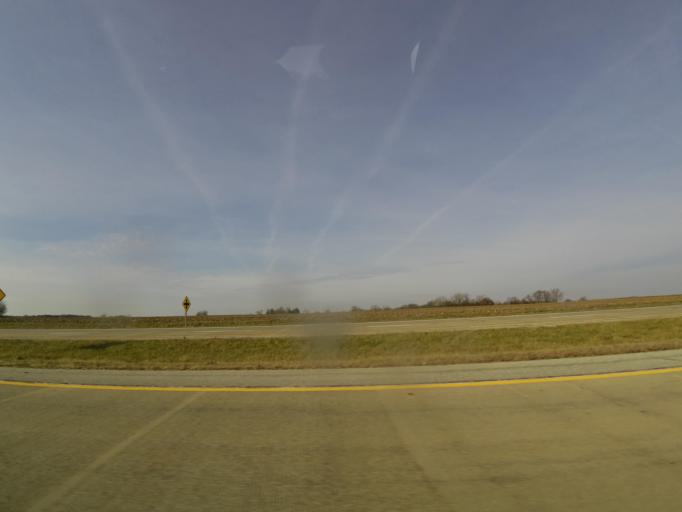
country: US
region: Illinois
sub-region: De Witt County
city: Clinton
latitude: 40.1624
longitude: -88.9821
